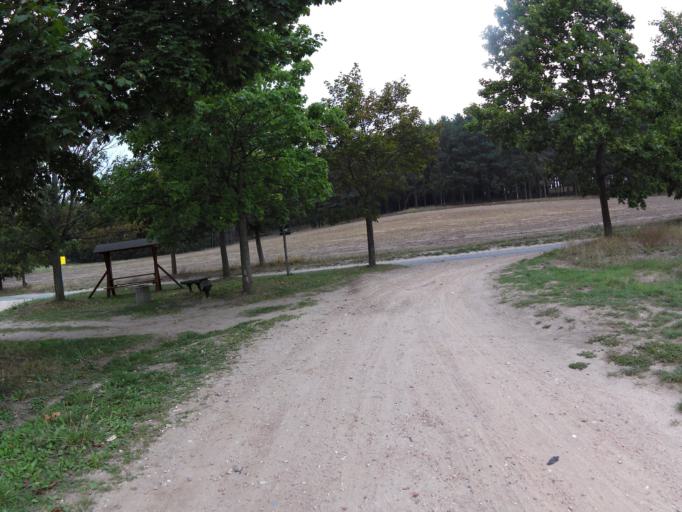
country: DE
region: Mecklenburg-Vorpommern
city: Seebad Heringsdorf
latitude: 53.9438
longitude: 14.1438
